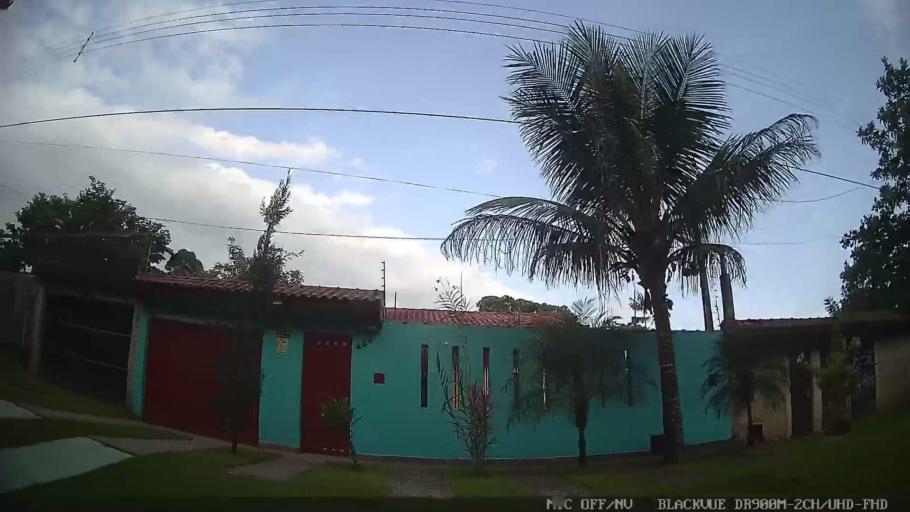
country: BR
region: Sao Paulo
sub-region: Bertioga
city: Bertioga
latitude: -23.8077
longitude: -46.0641
